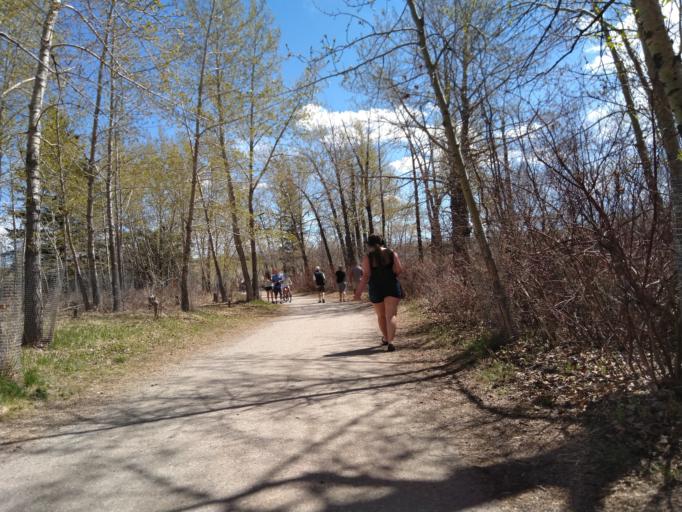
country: CA
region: Alberta
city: Calgary
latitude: 51.0996
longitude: -114.2118
